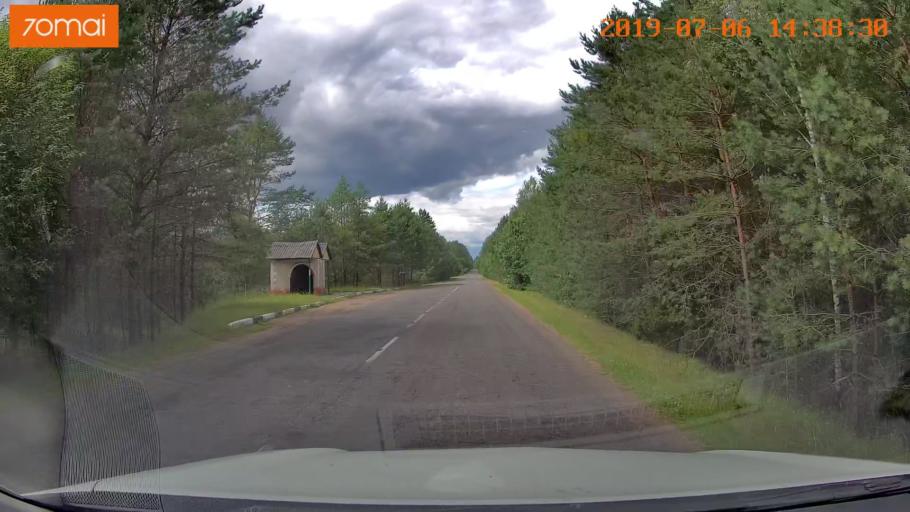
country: BY
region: Minsk
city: Ivyanyets
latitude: 53.9067
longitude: 26.7020
